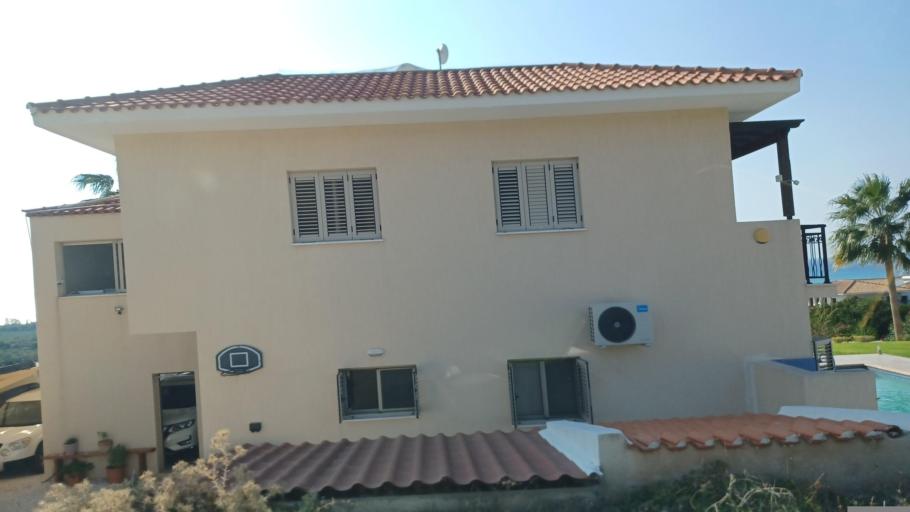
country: CY
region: Pafos
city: Kissonerga
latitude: 34.8453
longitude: 32.3950
